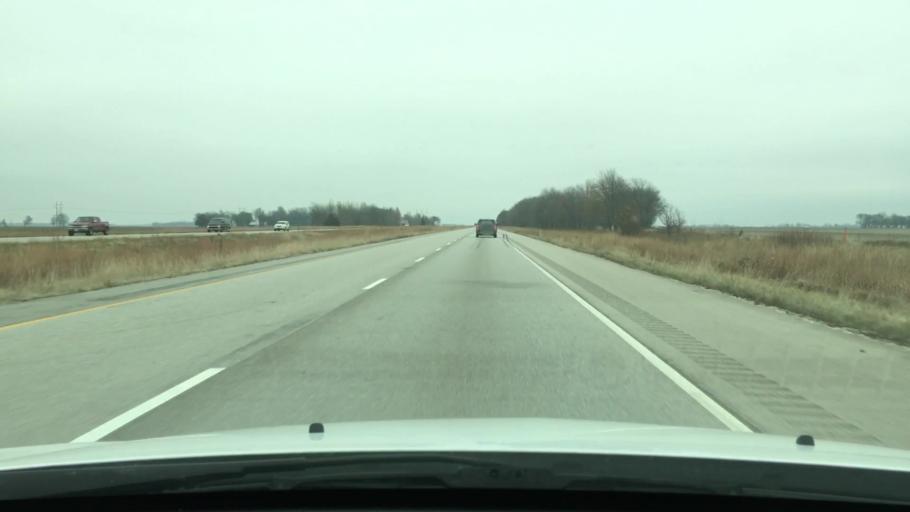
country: US
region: Illinois
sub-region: Sangamon County
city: New Berlin
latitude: 39.7368
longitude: -90.0271
